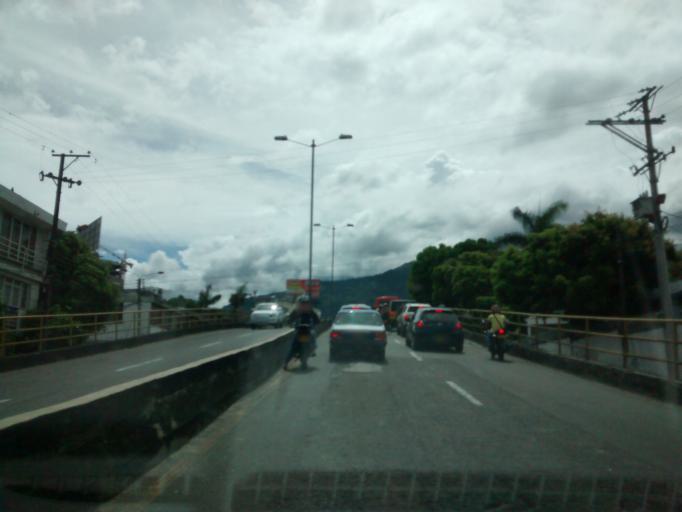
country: CO
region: Tolima
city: Ibague
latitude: 4.4350
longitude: -75.2023
